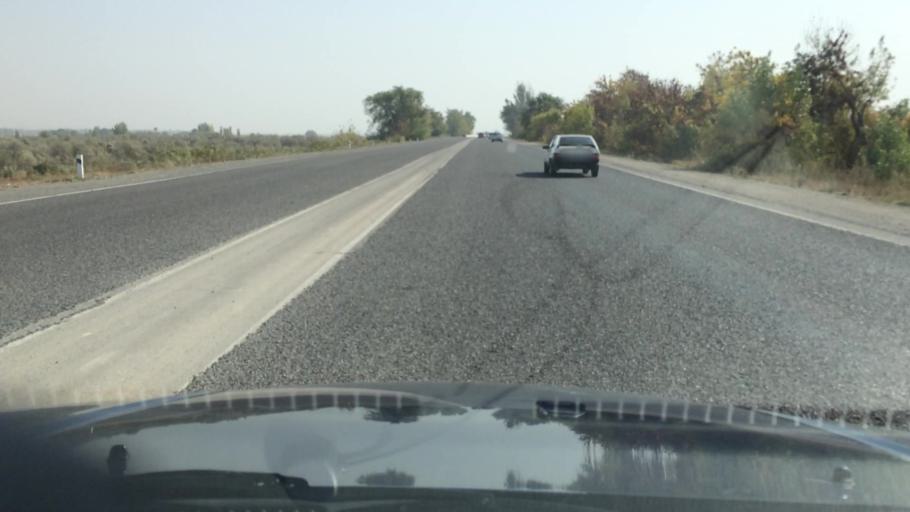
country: KG
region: Chuy
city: Kant
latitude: 42.9556
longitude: 74.9371
